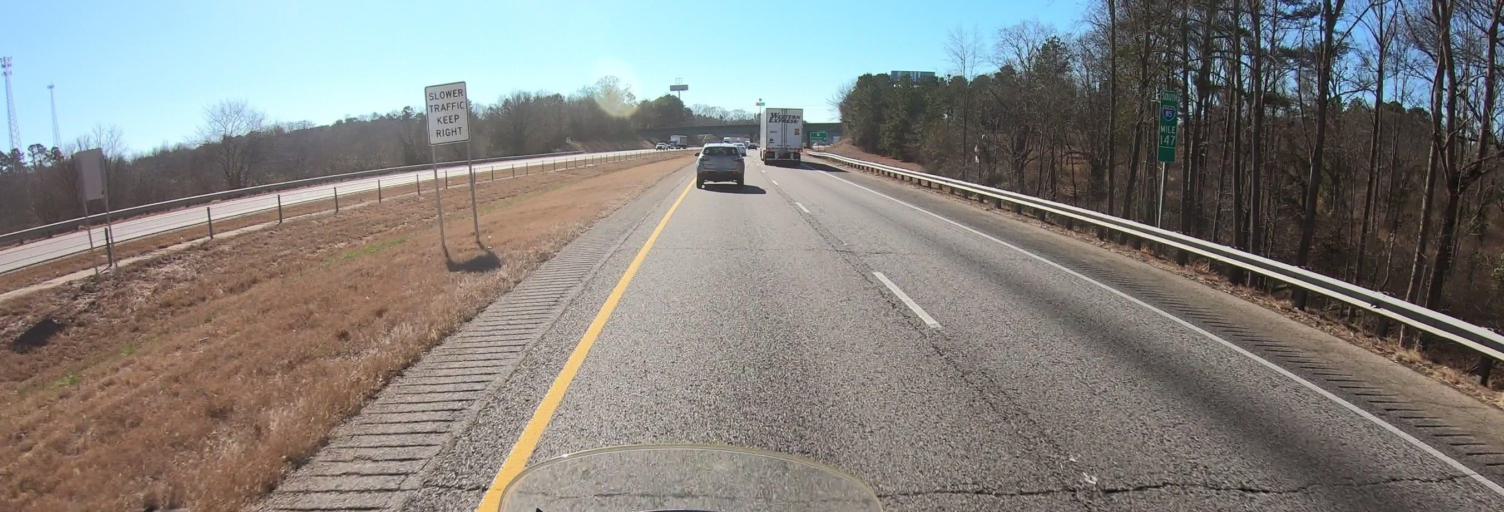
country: US
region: Georgia
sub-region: Jackson County
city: Commerce
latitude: 34.2316
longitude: -83.4953
